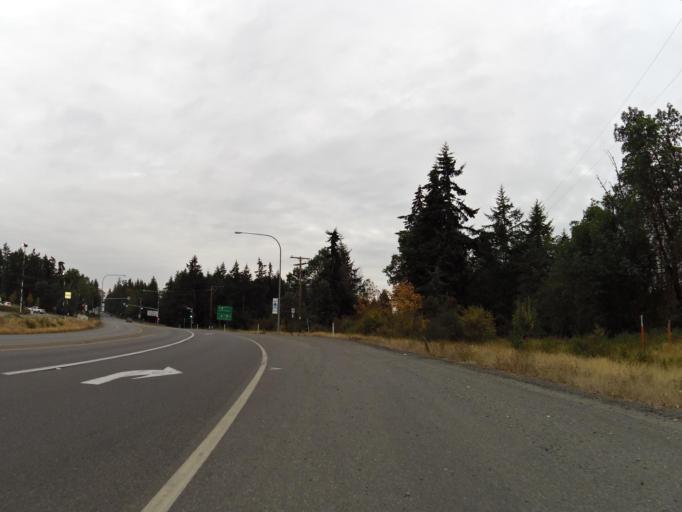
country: US
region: Washington
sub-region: Jefferson County
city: Port Hadlock-Irondale
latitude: 48.0724
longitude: -122.8188
